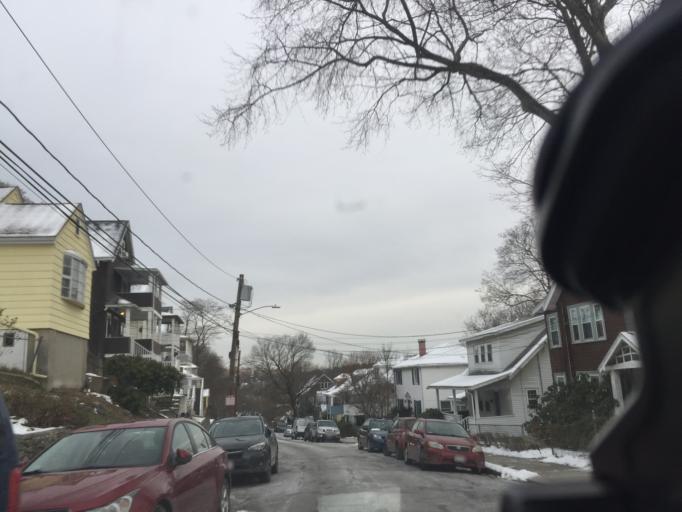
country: US
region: Massachusetts
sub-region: Middlesex County
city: Watertown
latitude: 42.3475
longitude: -71.1678
